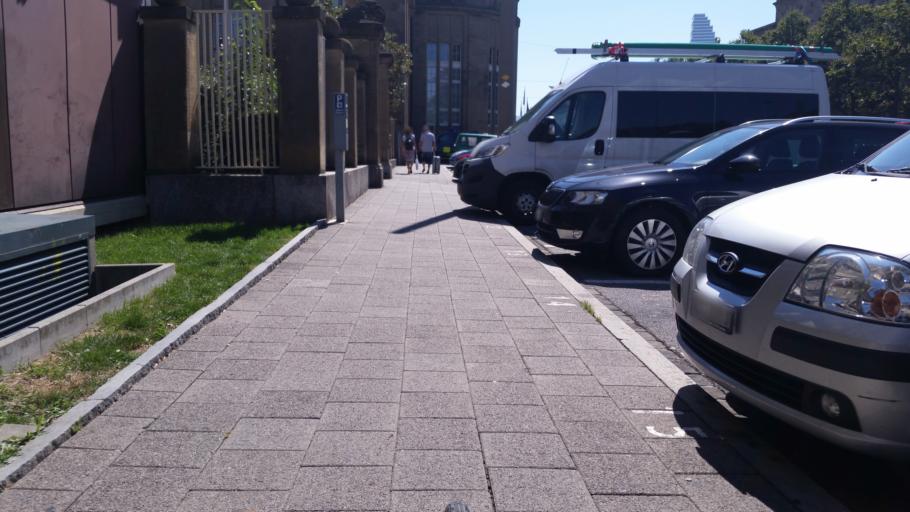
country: CH
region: Basel-Landschaft
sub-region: Bezirk Arlesheim
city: Birsfelden
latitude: 47.5685
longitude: 7.6060
